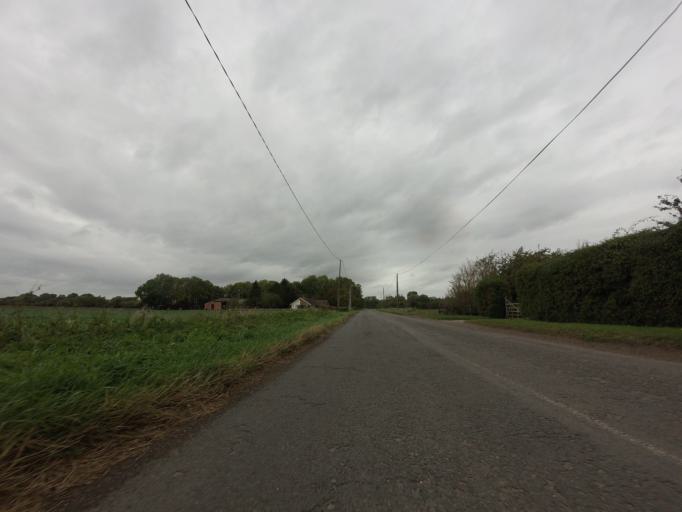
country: GB
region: England
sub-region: Cambridgeshire
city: Meldreth
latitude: 52.1183
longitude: 0.0259
